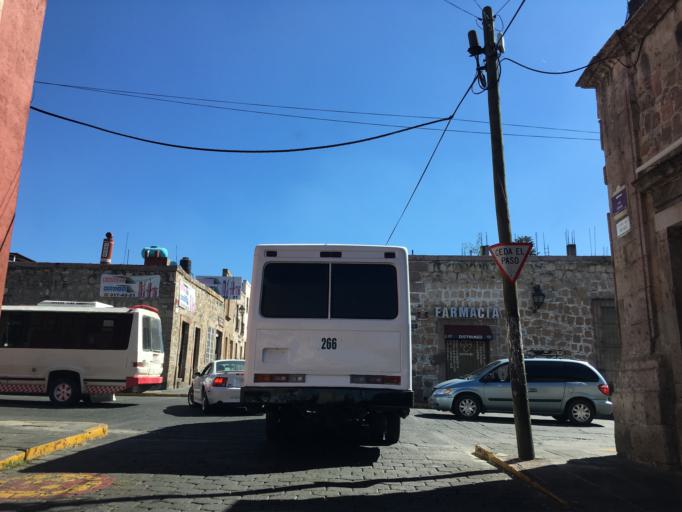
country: MX
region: Michoacan
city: Morelia
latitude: 19.7021
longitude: -101.2004
